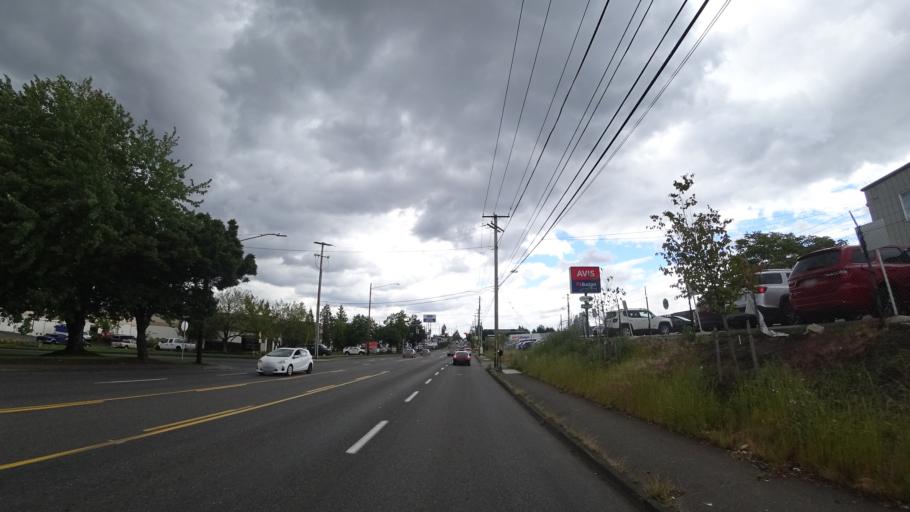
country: US
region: Oregon
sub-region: Multnomah County
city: Portland
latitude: 45.5686
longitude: -122.6019
